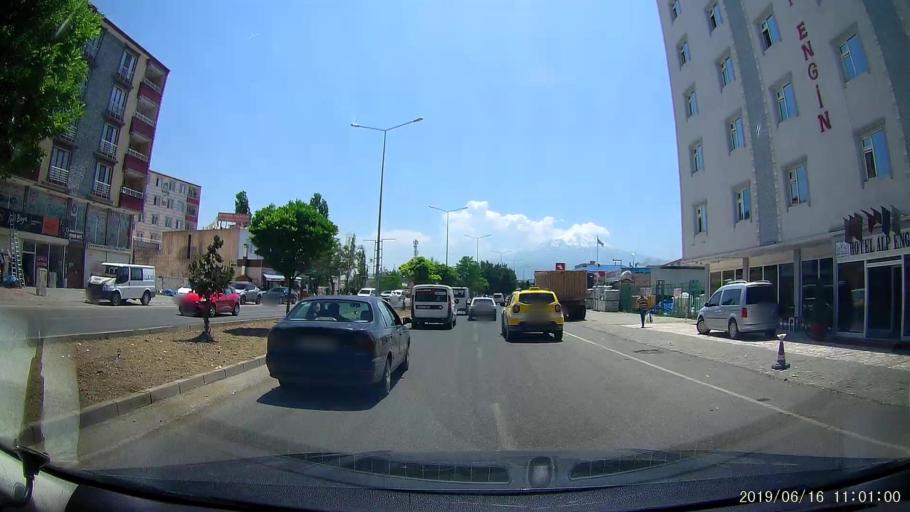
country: TR
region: Igdir
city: Igdir
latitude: 39.9173
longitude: 44.0468
